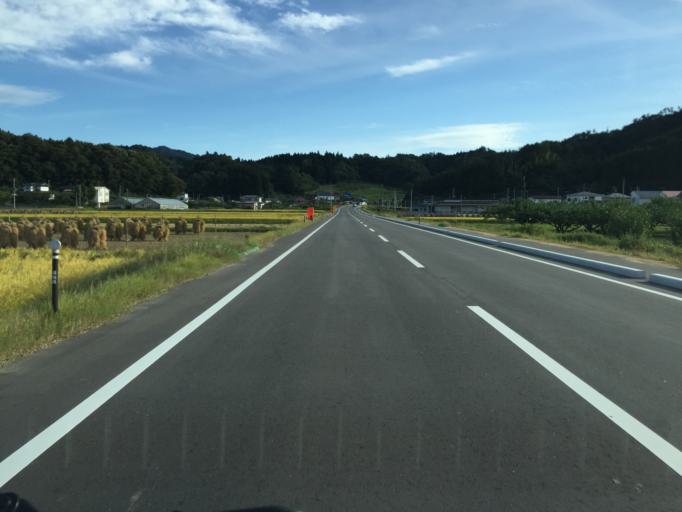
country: JP
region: Fukushima
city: Hobaramachi
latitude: 37.7459
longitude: 140.6075
